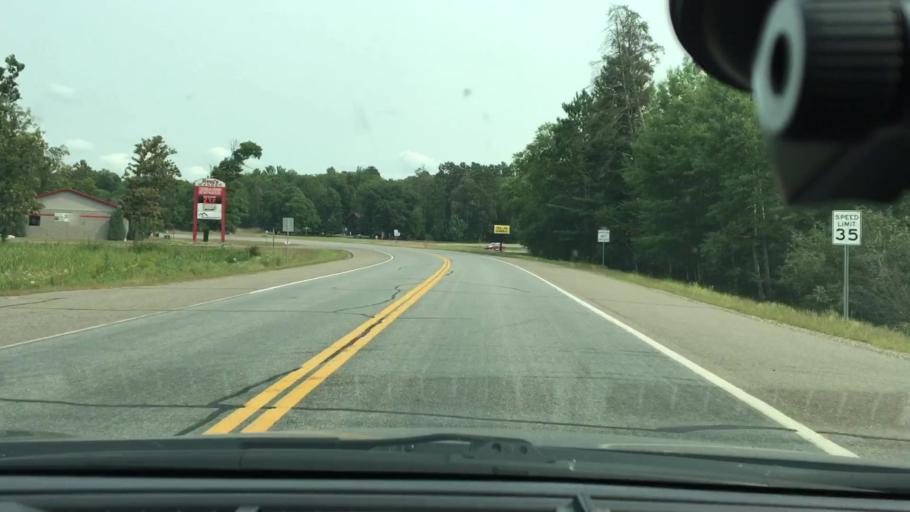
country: US
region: Minnesota
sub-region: Crow Wing County
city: Cross Lake
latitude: 46.6685
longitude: -94.1065
